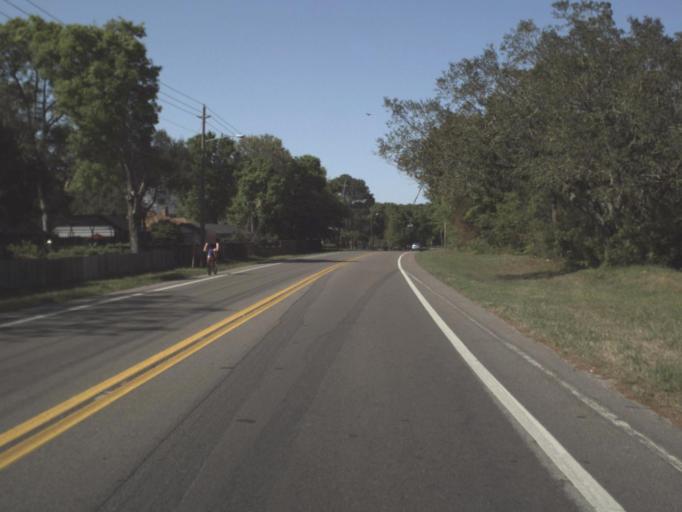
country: US
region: Florida
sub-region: Escambia County
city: East Pensacola Heights
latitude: 30.4438
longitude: -87.1735
